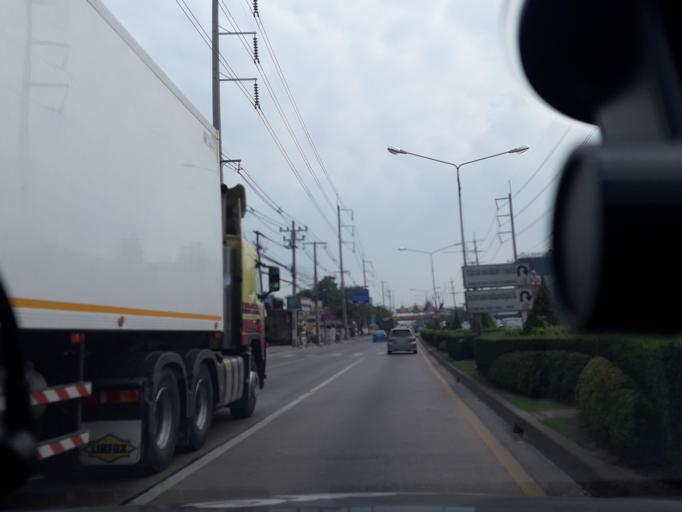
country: TH
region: Pathum Thani
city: Lam Luk Ka
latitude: 13.9342
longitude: 100.7237
